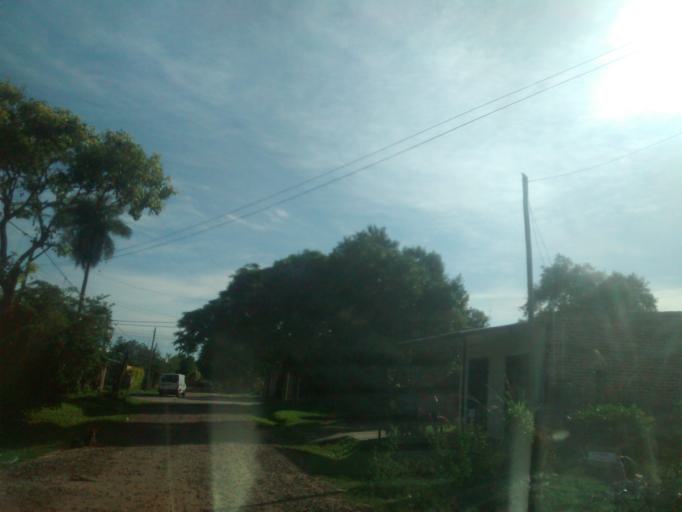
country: AR
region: Chaco
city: Puerto Tirol
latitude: -27.3758
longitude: -59.0937
